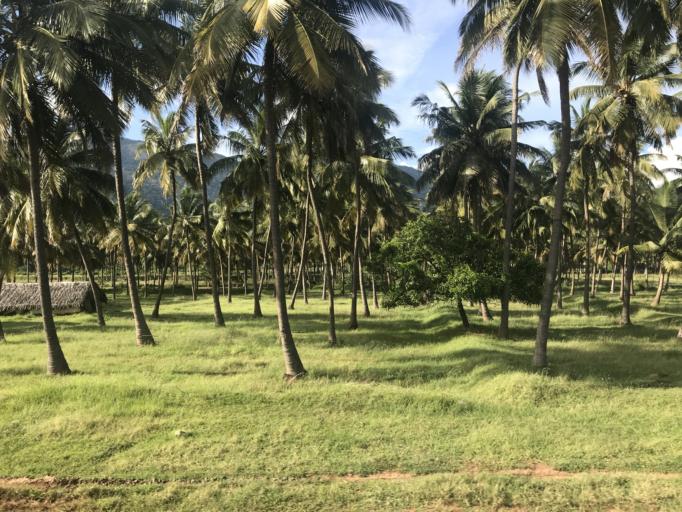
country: IN
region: Tamil Nadu
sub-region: Coimbatore
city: Madukkarai
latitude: 10.8771
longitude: 76.8612
